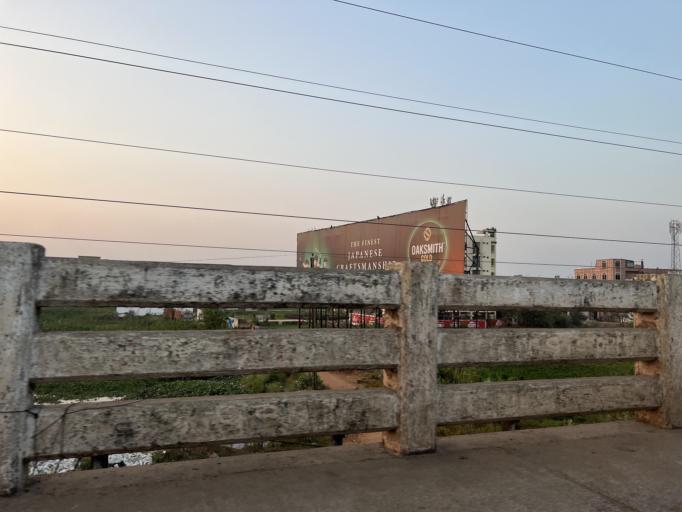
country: IN
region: Odisha
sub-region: Khordha
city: Bhubaneshwar
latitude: 20.3060
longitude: 85.8688
